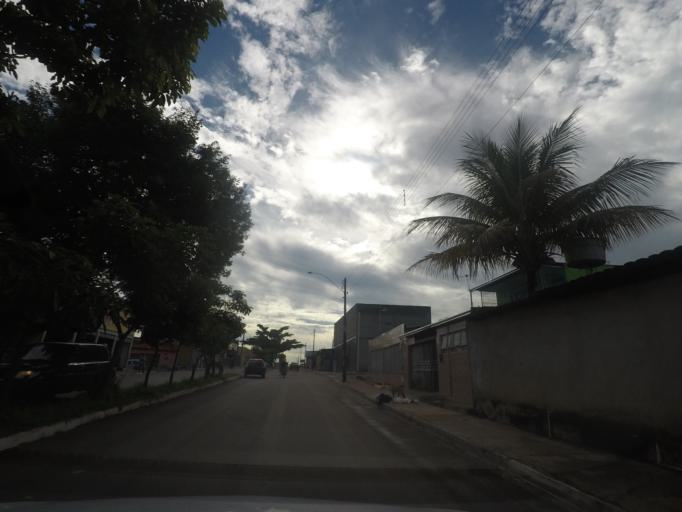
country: BR
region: Goias
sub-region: Aparecida De Goiania
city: Aparecida de Goiania
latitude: -16.8165
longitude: -49.3168
